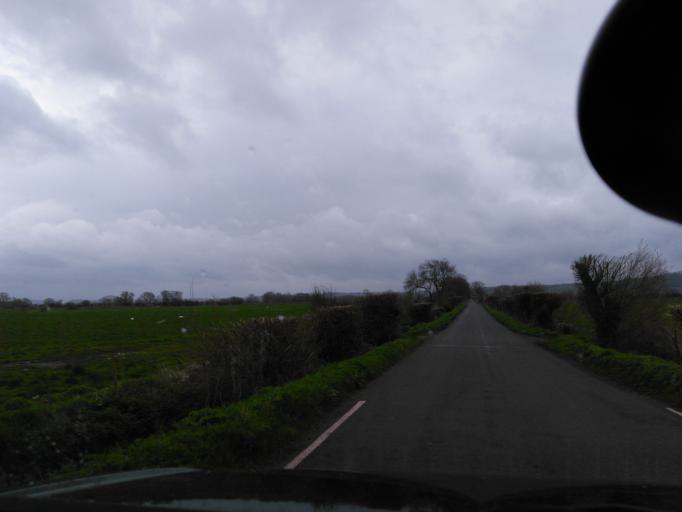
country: GB
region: England
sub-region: Somerset
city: Langport
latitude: 51.1078
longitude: -2.8197
